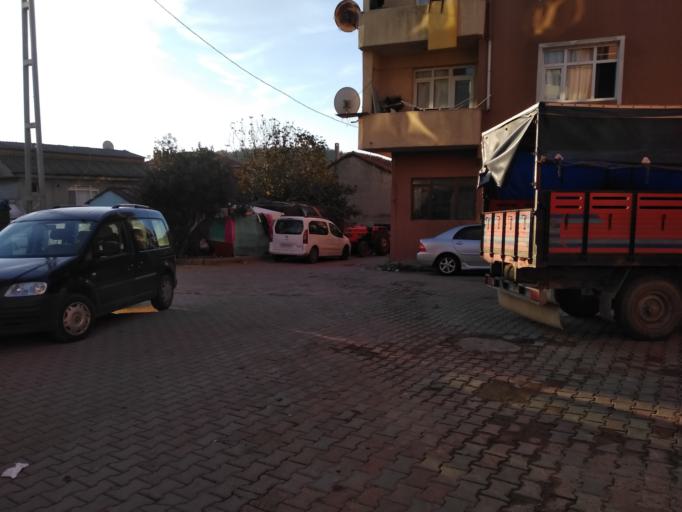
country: TR
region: Istanbul
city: Arikoey
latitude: 41.2372
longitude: 28.9836
